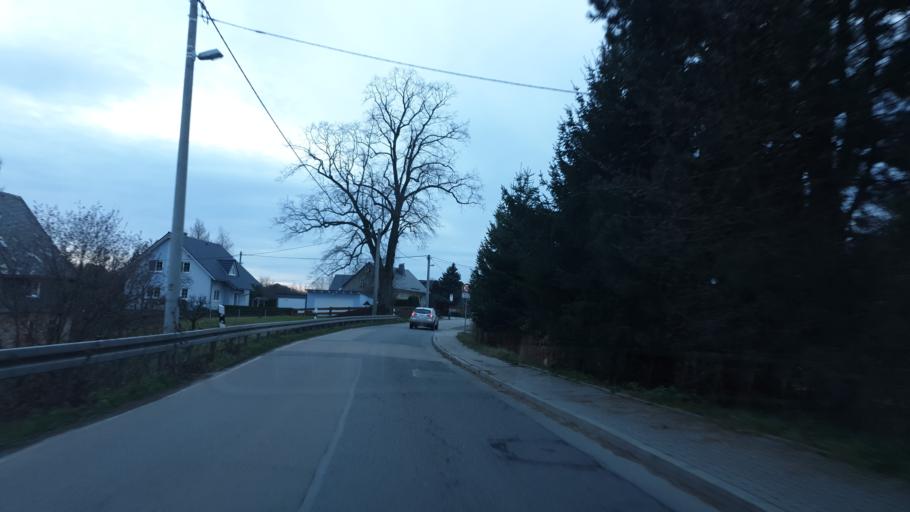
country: DE
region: Saxony
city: Hartenstein
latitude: 50.6885
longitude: 12.6703
